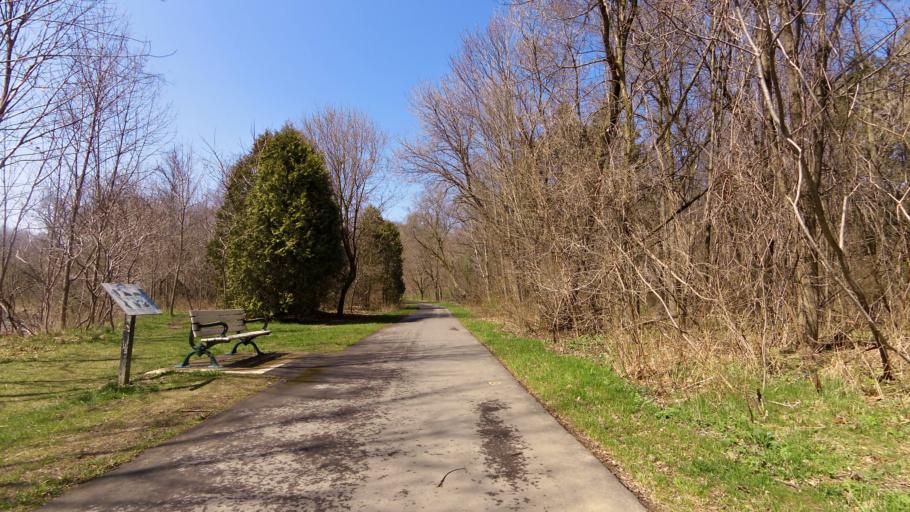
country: CA
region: Ontario
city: Etobicoke
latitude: 43.5988
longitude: -79.5536
